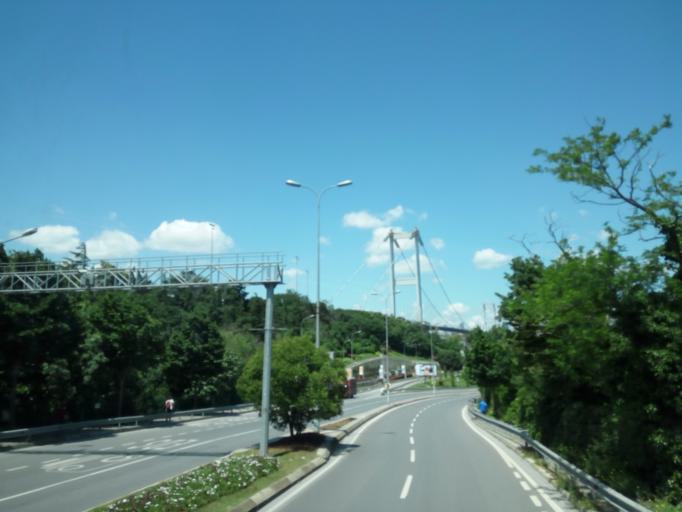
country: TR
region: Istanbul
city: UEskuedar
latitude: 41.0386
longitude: 29.0437
